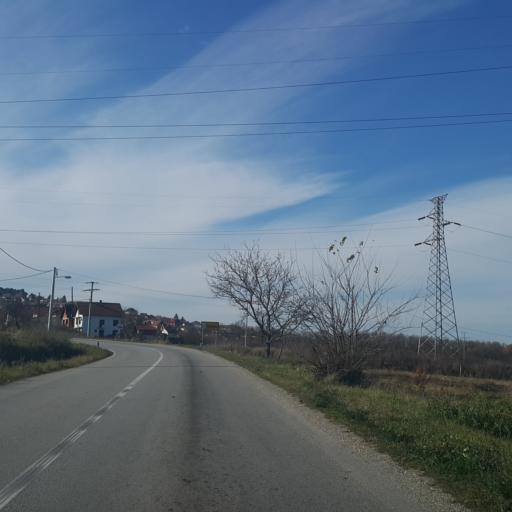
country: RS
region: Central Serbia
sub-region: Sumadijski Okrug
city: Topola
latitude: 44.2493
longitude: 20.6994
